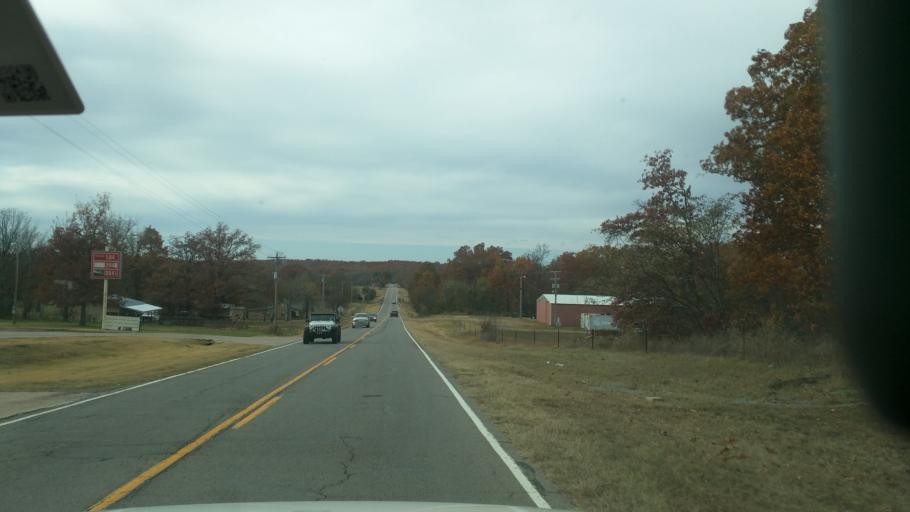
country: US
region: Oklahoma
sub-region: Cherokee County
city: Tahlequah
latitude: 35.9300
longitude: -94.8575
